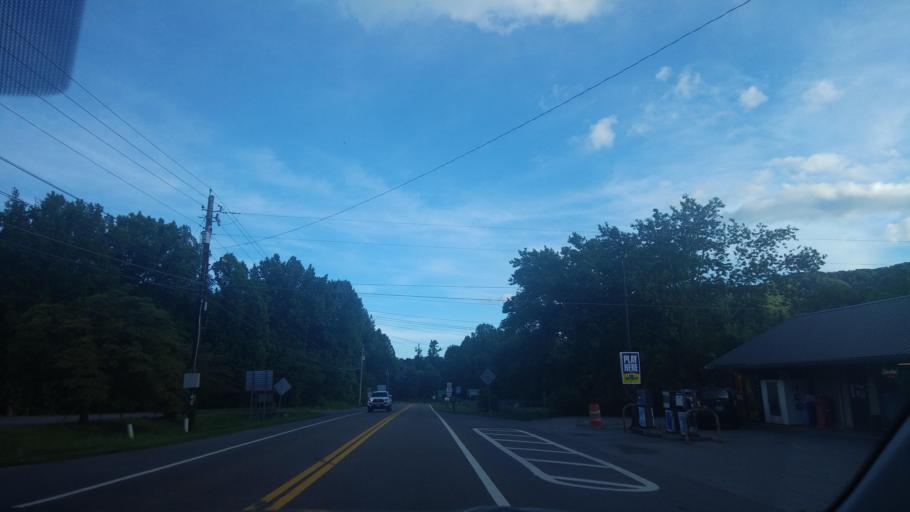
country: US
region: Tennessee
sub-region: Cocke County
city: Newport
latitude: 35.7947
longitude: -83.2366
